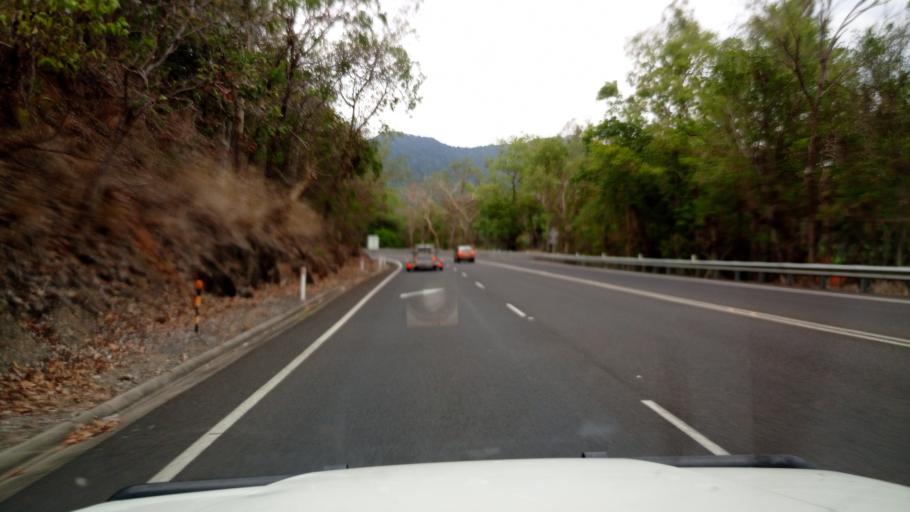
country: AU
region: Queensland
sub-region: Cairns
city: Redlynch
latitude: -16.8375
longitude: 145.6862
